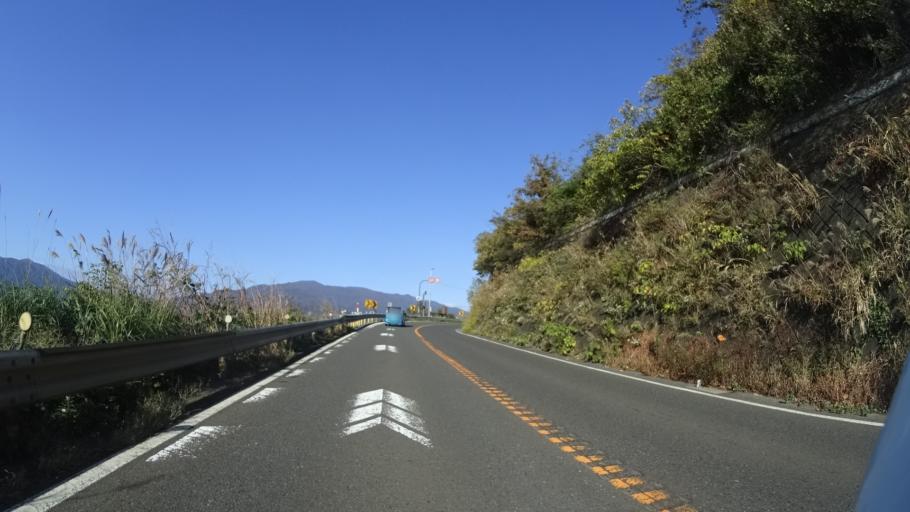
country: JP
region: Fukui
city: Tsuruga
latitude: 35.6888
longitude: 136.0825
